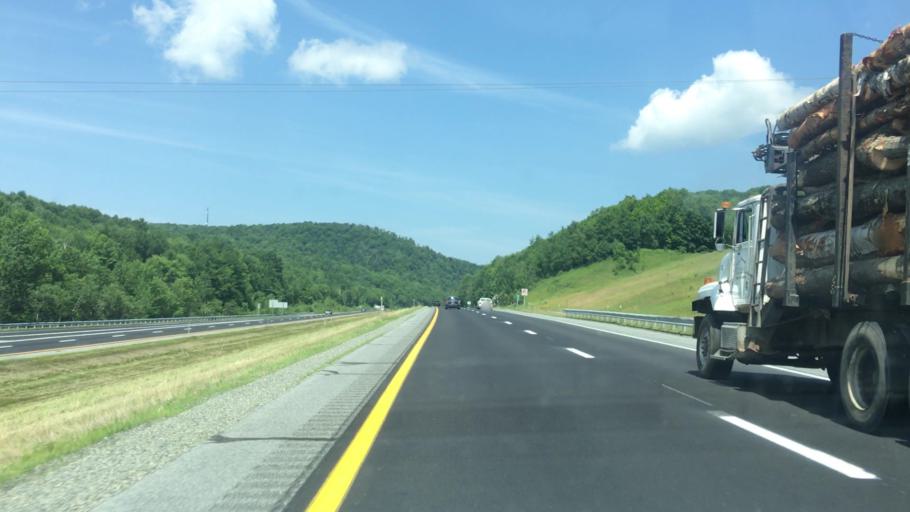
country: US
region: New Hampshire
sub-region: Grafton County
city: Enfield
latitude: 43.5680
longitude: -72.1507
